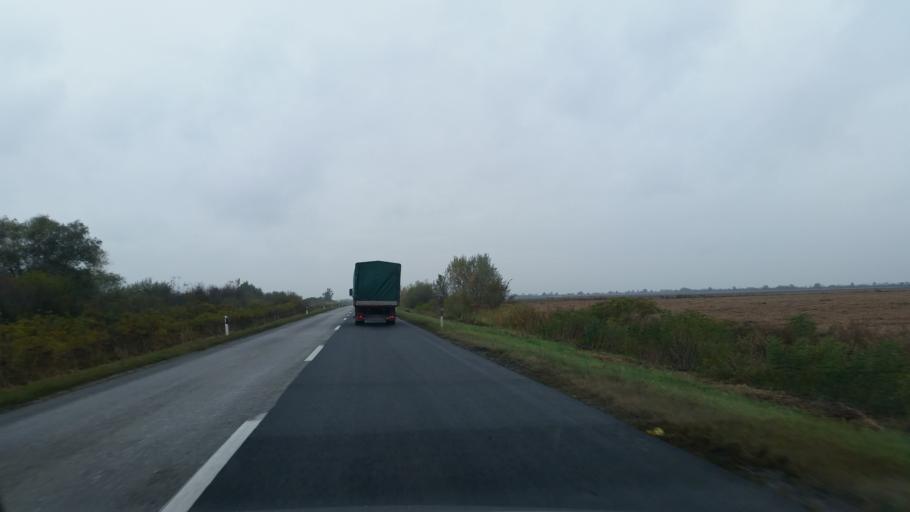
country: RS
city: Sefkerin
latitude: 44.9578
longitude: 20.4255
